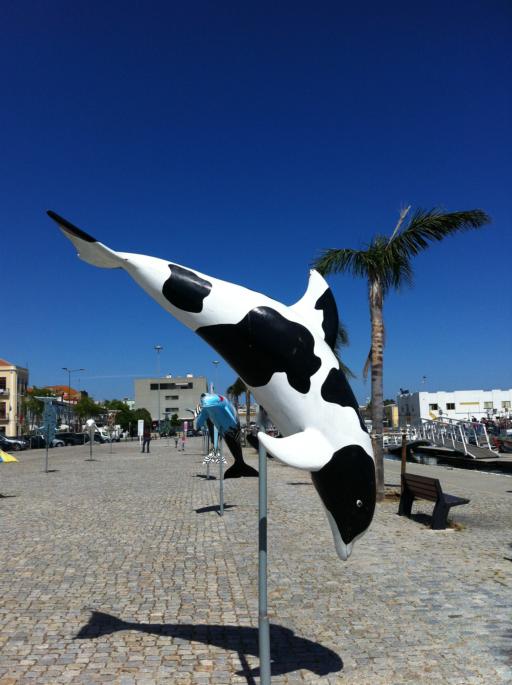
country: PT
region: Setubal
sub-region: Setubal
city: Setubal
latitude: 38.5202
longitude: -8.8998
